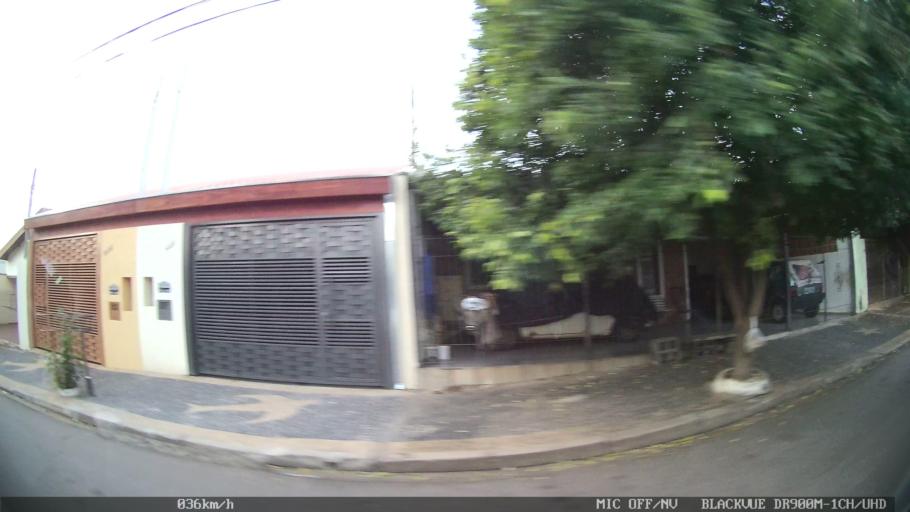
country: BR
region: Sao Paulo
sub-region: Sumare
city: Sumare
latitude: -22.8142
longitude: -47.2741
